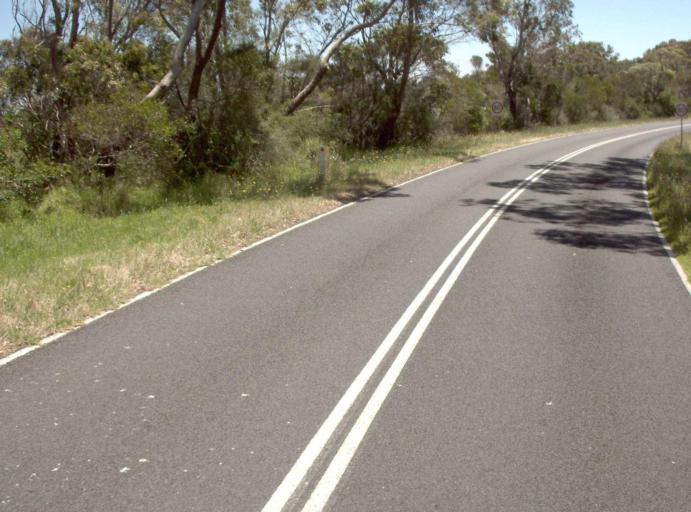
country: AU
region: Victoria
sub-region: Latrobe
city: Morwell
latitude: -38.8537
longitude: 146.2449
